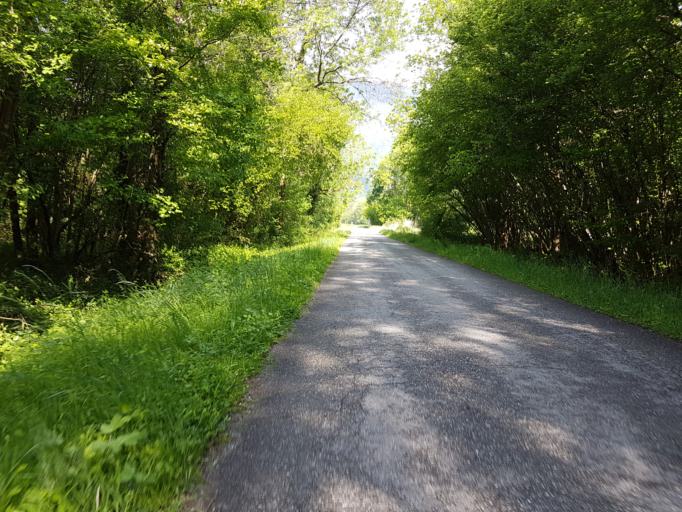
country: FR
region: Rhone-Alpes
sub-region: Departement de l'Ain
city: Culoz
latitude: 45.8525
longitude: 5.8157
